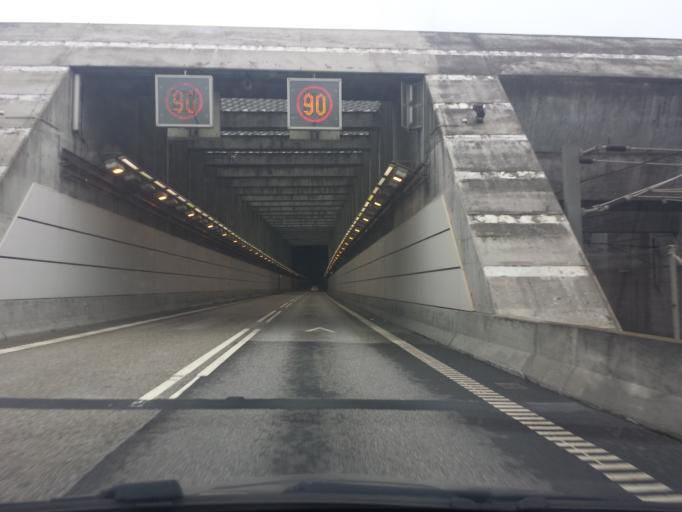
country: DK
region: Capital Region
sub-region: Dragor Kommune
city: Dragor
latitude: 55.6312
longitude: 12.6770
